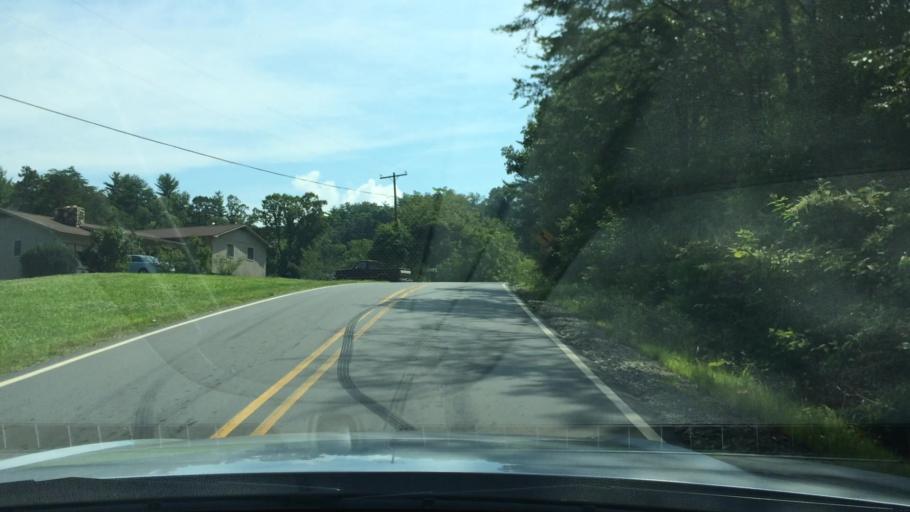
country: US
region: North Carolina
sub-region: Buncombe County
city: Weaverville
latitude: 35.6805
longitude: -82.5898
